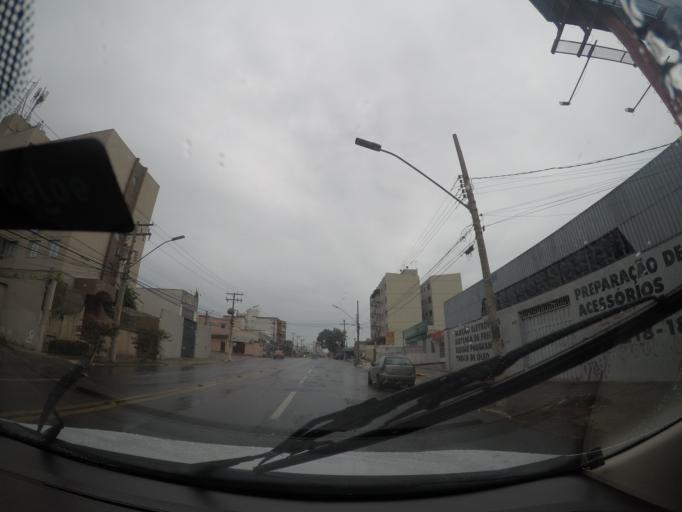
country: BR
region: Goias
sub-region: Goiania
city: Goiania
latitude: -16.6859
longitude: -49.2480
